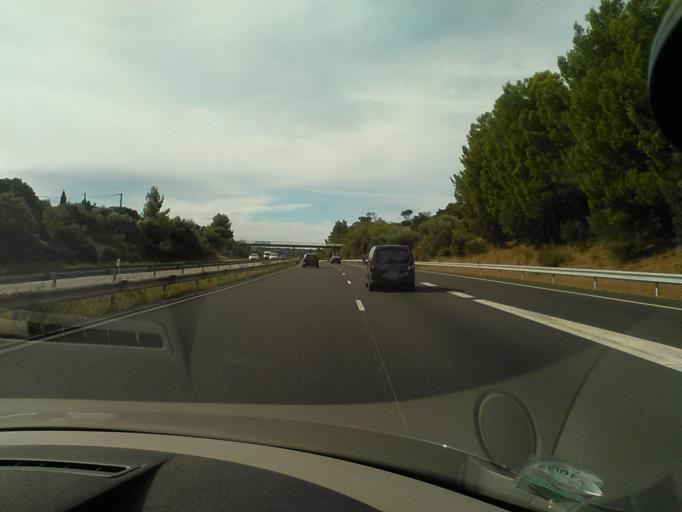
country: FR
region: Languedoc-Roussillon
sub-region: Departement du Gard
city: Roquemaure
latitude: 44.0479
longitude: 4.7645
